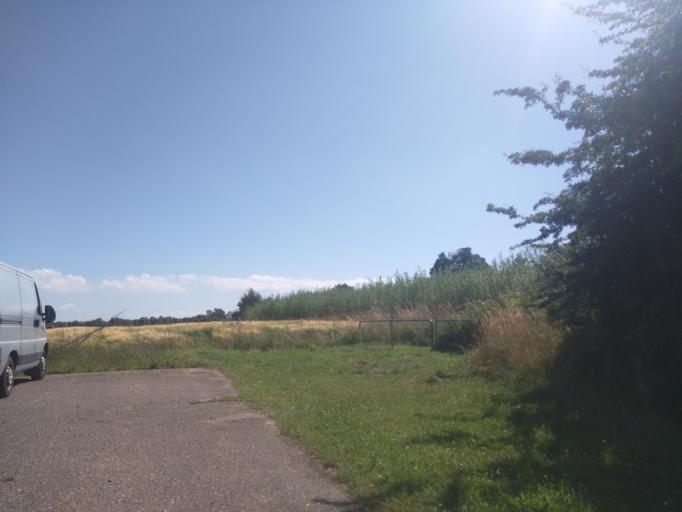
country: DK
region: Zealand
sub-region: Kalundborg Kommune
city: Svebolle
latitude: 55.6920
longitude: 11.2688
